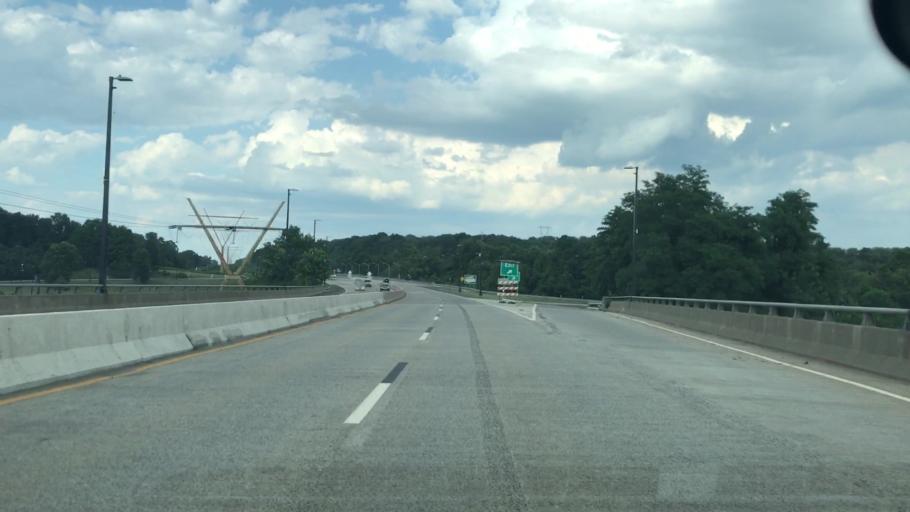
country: US
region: Pennsylvania
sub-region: Bucks County
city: New Hope
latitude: 40.3802
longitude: -74.9528
